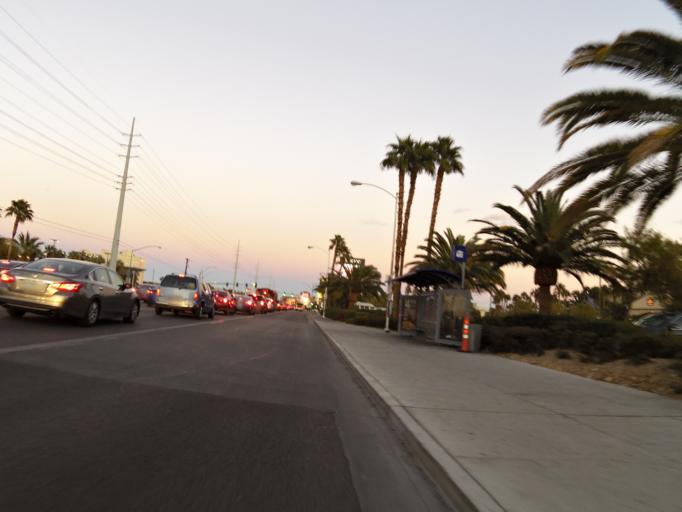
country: US
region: Nevada
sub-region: Clark County
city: Paradise
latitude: 36.1143
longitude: -115.1611
